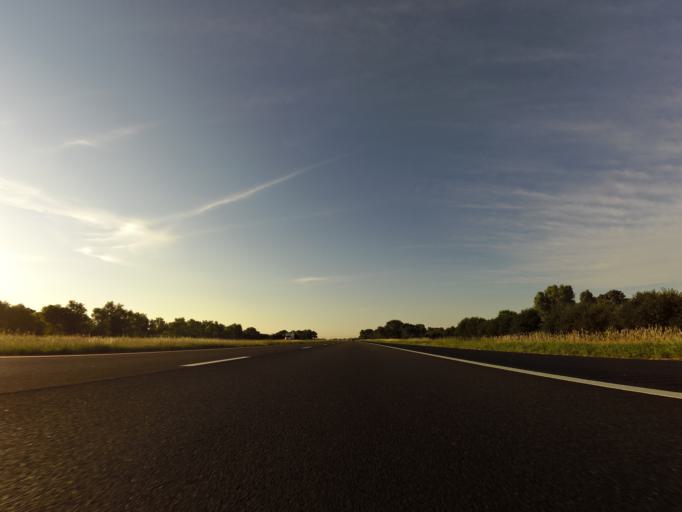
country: US
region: Kansas
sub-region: Sedgwick County
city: Colwich
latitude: 37.8145
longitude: -97.5055
